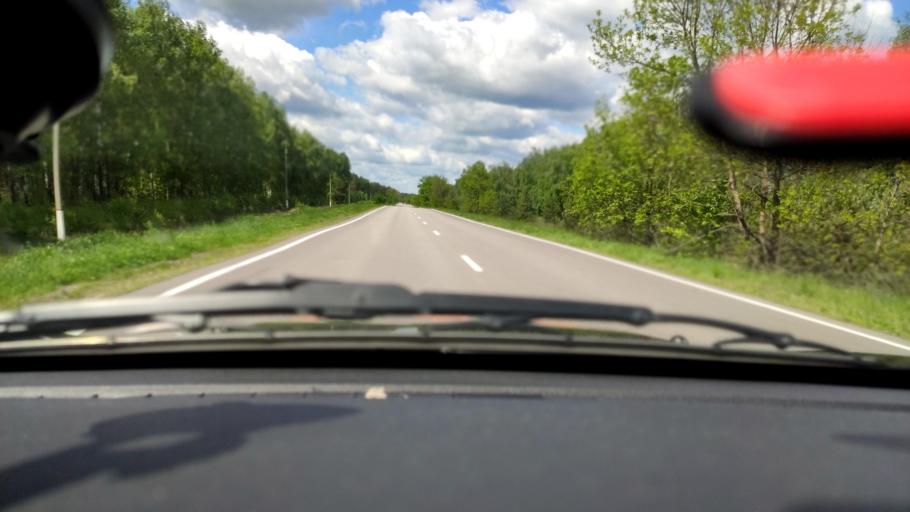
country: RU
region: Belgorod
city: Krasnoye
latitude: 51.0564
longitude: 38.8712
